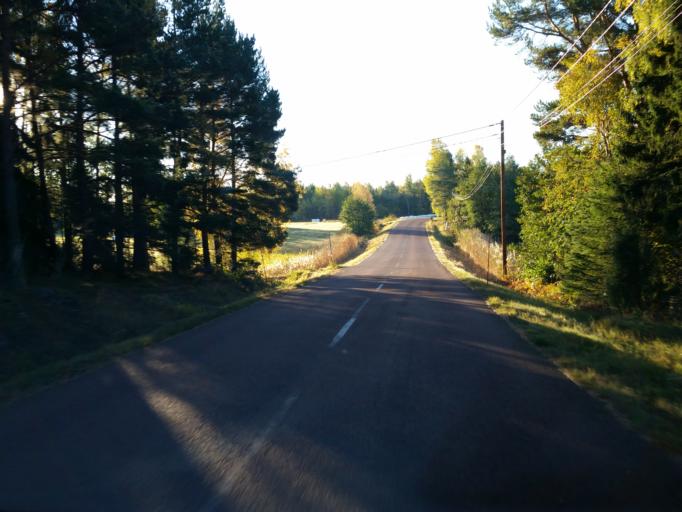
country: AX
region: Alands skaergard
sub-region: Vardoe
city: Vardoe
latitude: 60.2967
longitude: 20.3845
